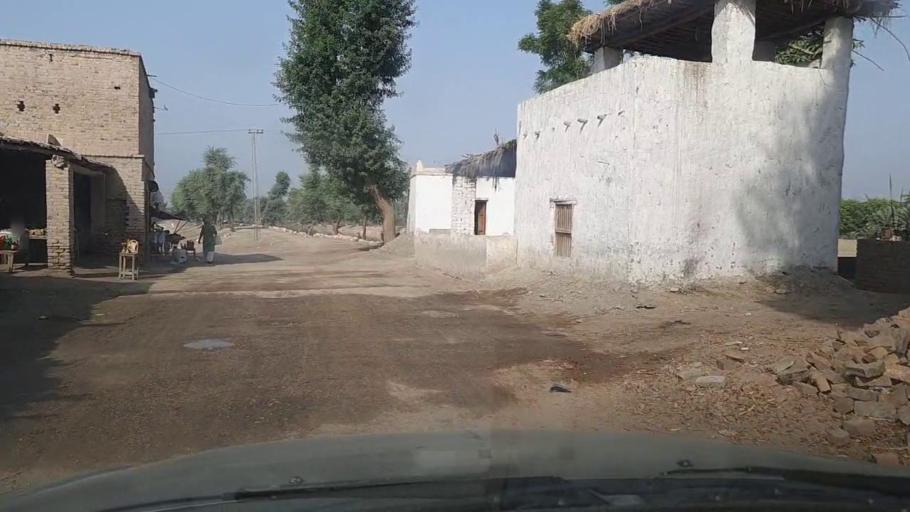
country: PK
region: Sindh
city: Pir jo Goth
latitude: 27.5257
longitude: 68.4926
